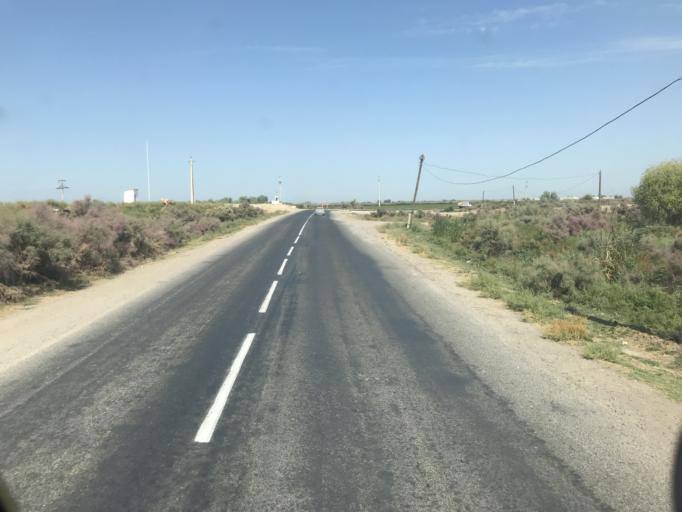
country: KZ
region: Ongtustik Qazaqstan
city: Myrzakent
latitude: 40.6793
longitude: 68.5335
